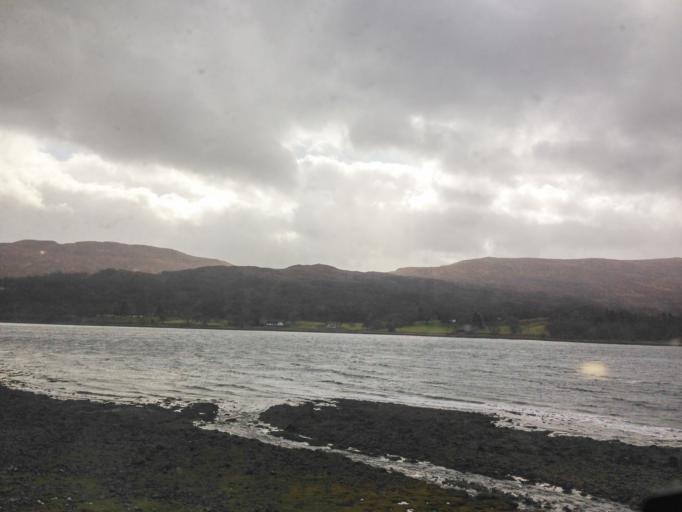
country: GB
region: Scotland
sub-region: Highland
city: Fort William
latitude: 56.8521
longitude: -5.1732
